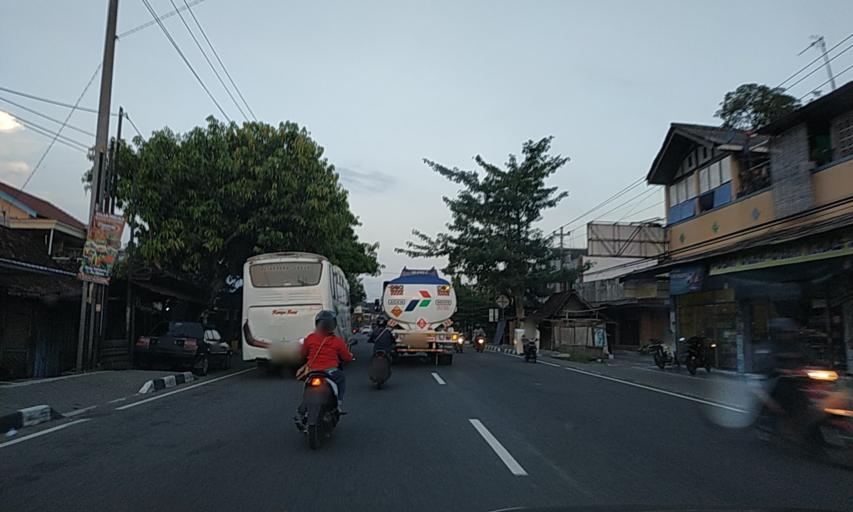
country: ID
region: Daerah Istimewa Yogyakarta
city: Srandakan
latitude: -7.8656
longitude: 110.1581
